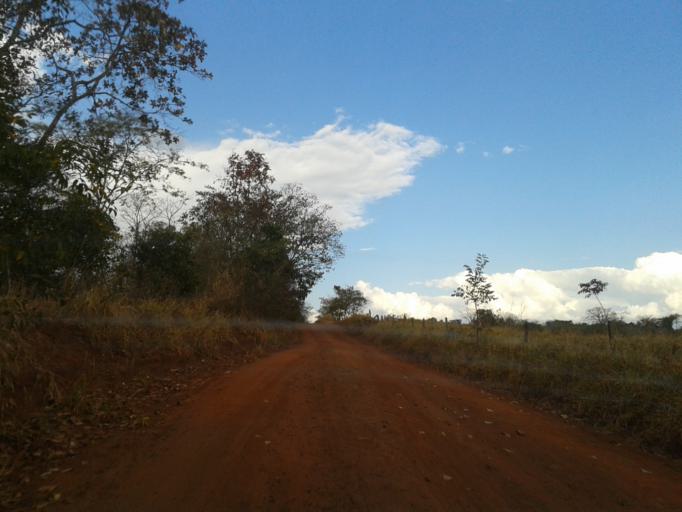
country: BR
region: Minas Gerais
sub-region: Santa Vitoria
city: Santa Vitoria
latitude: -19.1963
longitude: -49.9149
